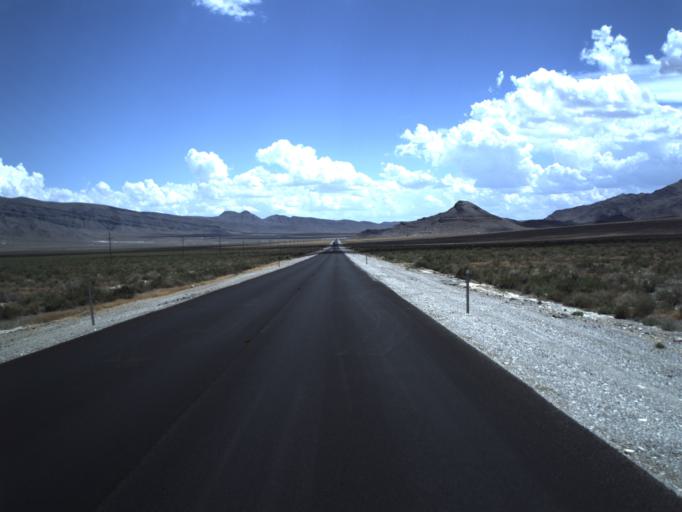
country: US
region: Utah
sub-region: Beaver County
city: Milford
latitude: 39.0814
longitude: -113.4904
